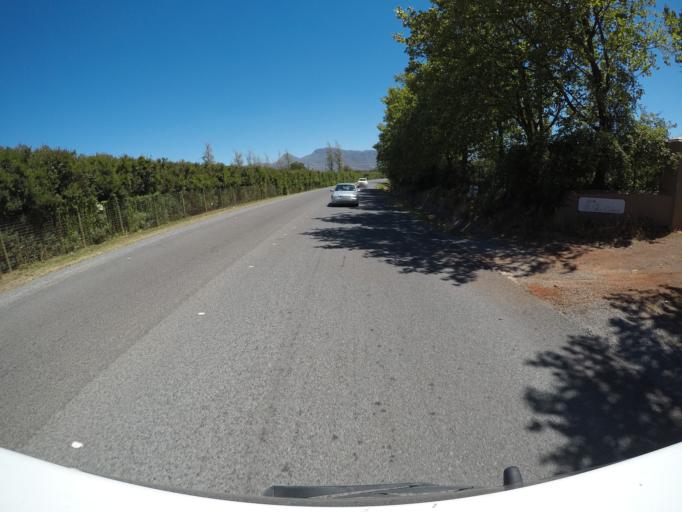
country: ZA
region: Western Cape
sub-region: Overberg District Municipality
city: Grabouw
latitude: -34.1772
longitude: 19.0348
